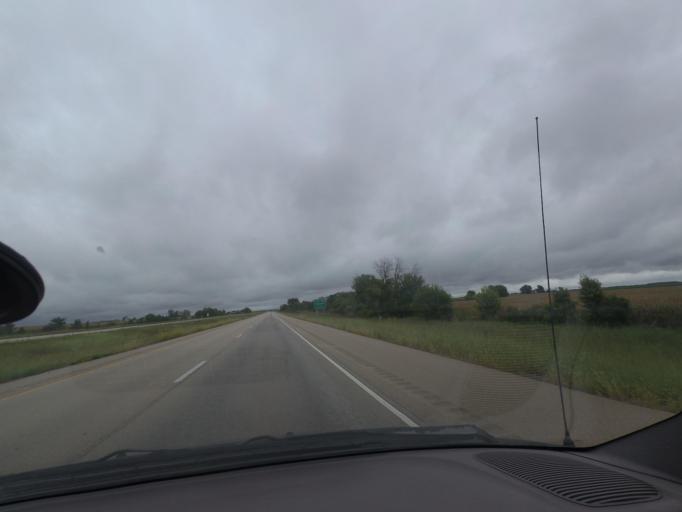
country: US
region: Illinois
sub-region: Piatt County
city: Cerro Gordo
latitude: 39.9447
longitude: -88.8311
